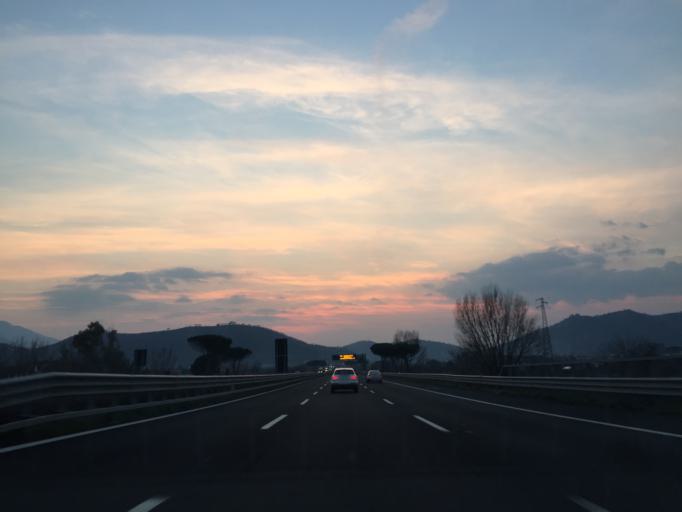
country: IT
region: Campania
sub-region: Provincia di Salerno
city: Roccapiemonte
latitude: 40.7676
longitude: 14.6955
